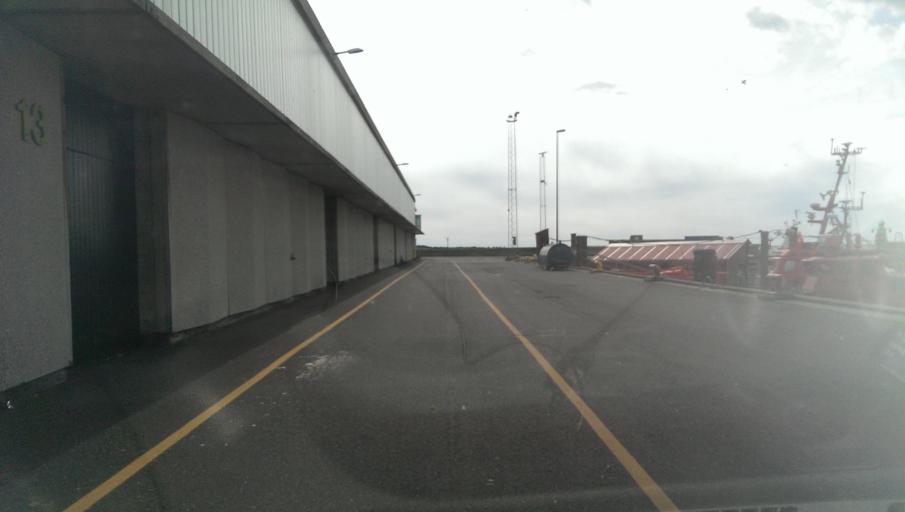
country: DK
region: South Denmark
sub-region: Esbjerg Kommune
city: Esbjerg
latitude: 55.4718
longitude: 8.4248
